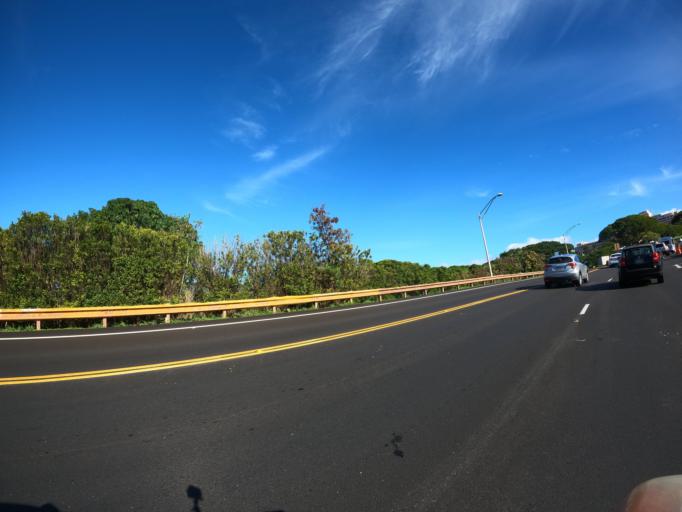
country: US
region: Hawaii
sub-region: Honolulu County
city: Halawa Heights
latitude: 21.3557
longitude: -157.8943
